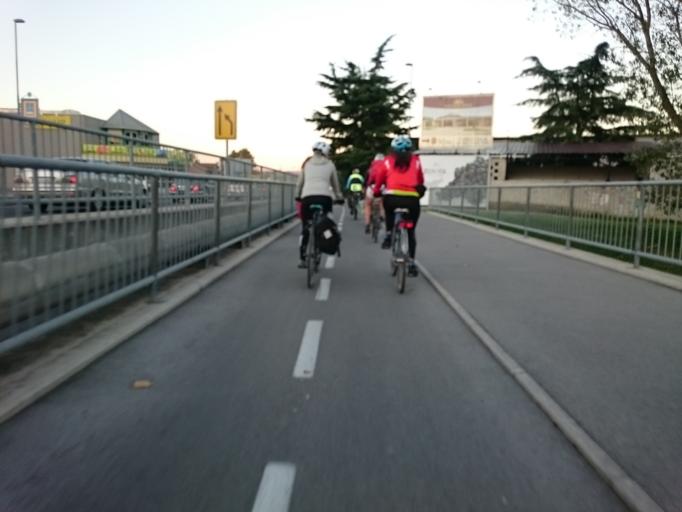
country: SI
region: Koper-Capodistria
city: Koper
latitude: 45.5347
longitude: 13.7357
